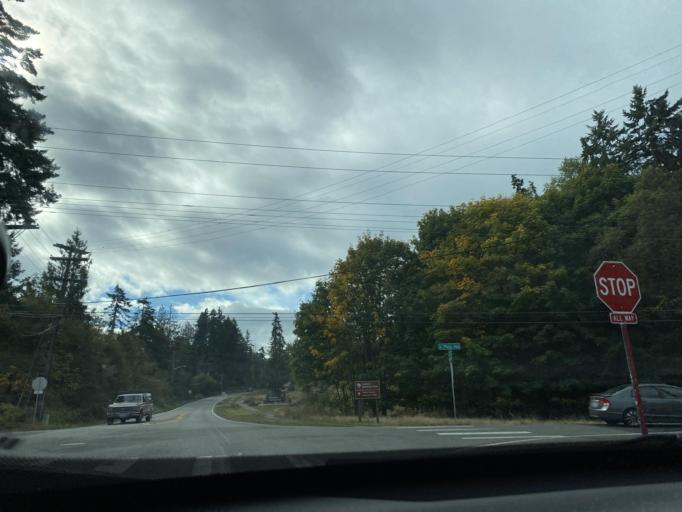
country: US
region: Washington
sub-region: Clallam County
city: Port Angeles
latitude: 48.1022
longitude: -123.4258
